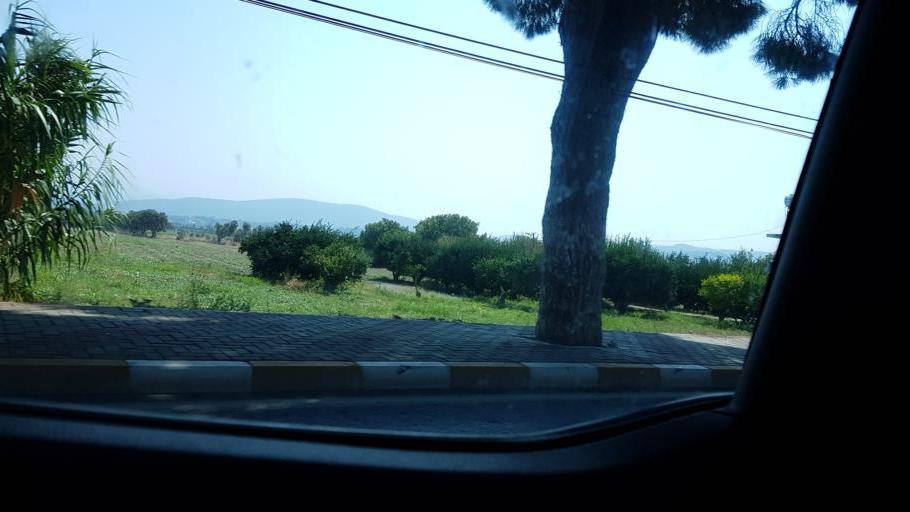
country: TR
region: Izmir
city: Urla
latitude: 38.3498
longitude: 26.7717
